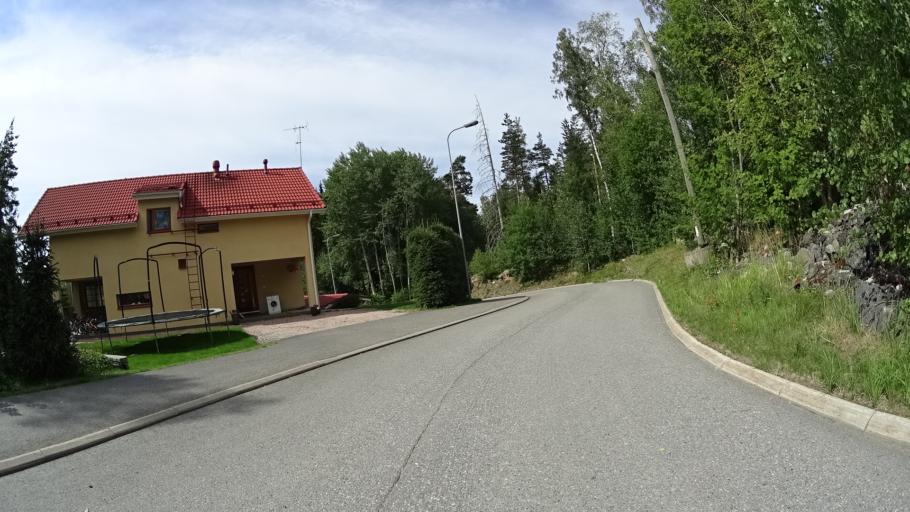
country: FI
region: Uusimaa
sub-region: Helsinki
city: Kauniainen
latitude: 60.1966
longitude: 24.7207
